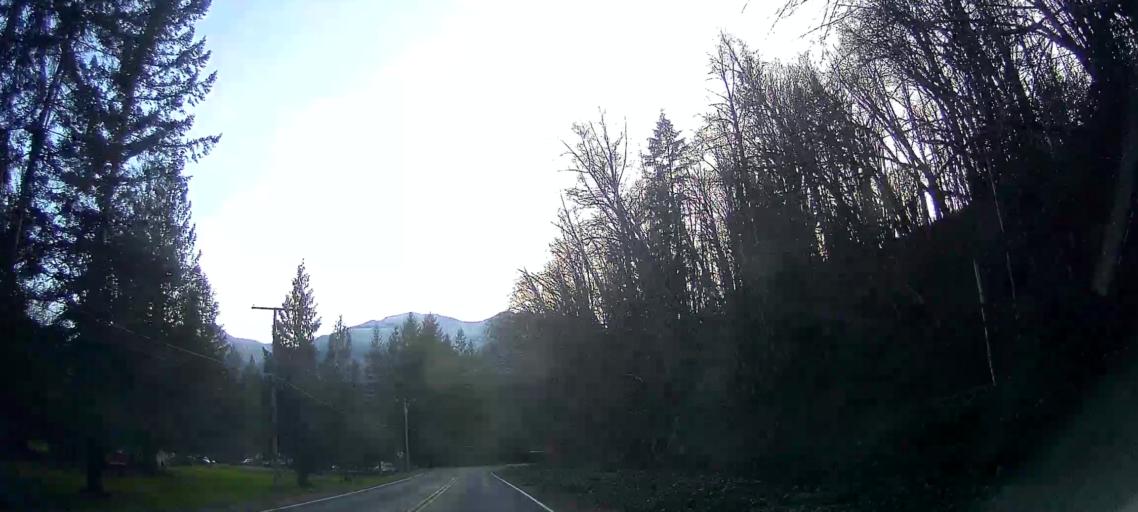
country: US
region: Washington
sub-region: Skagit County
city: Sedro-Woolley
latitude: 48.5364
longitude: -121.8851
